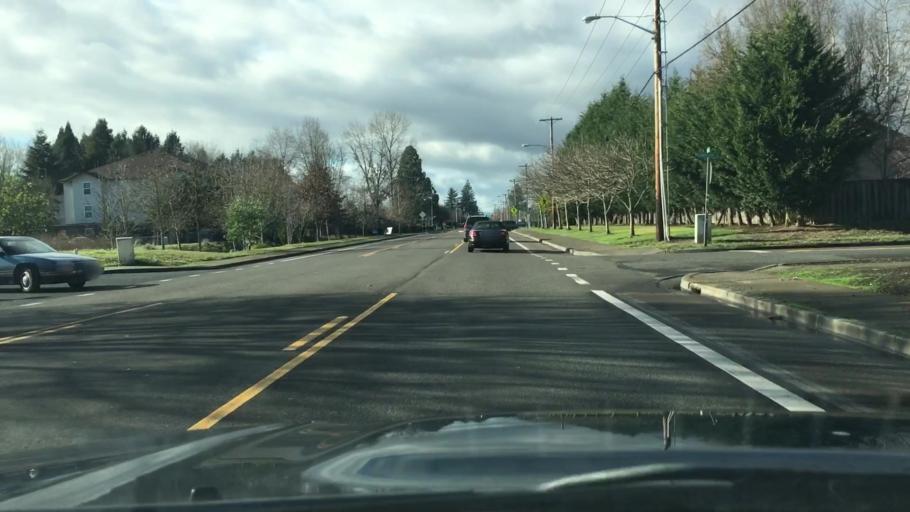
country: US
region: Oregon
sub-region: Lane County
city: Eugene
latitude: 44.0701
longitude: -123.1809
